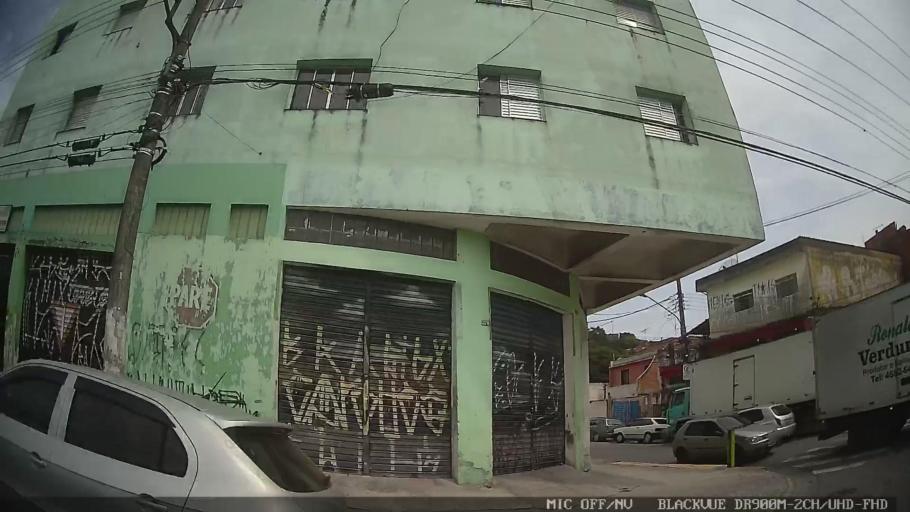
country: BR
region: Sao Paulo
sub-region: Ferraz De Vasconcelos
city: Ferraz de Vasconcelos
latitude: -23.5419
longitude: -46.3702
